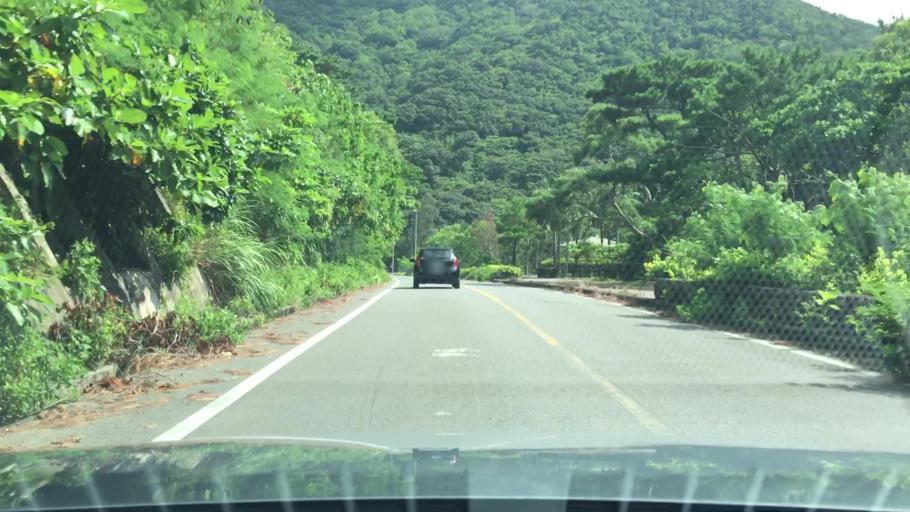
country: JP
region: Okinawa
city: Ishigaki
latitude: 24.4355
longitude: 124.2116
